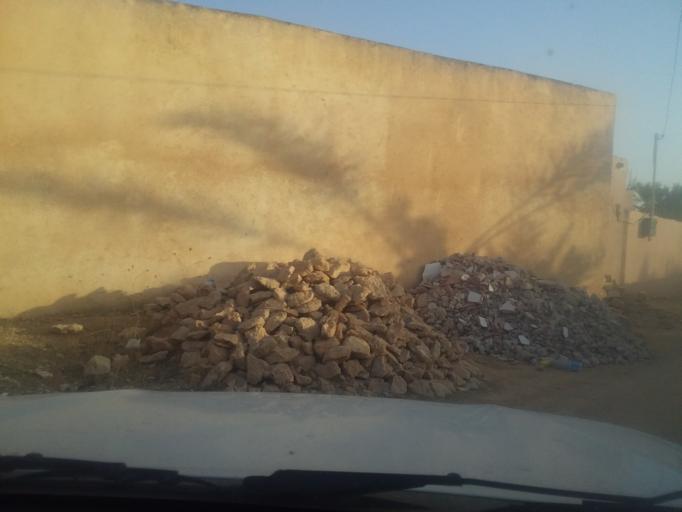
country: TN
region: Qabis
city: Gabes
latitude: 33.6293
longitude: 10.2959
